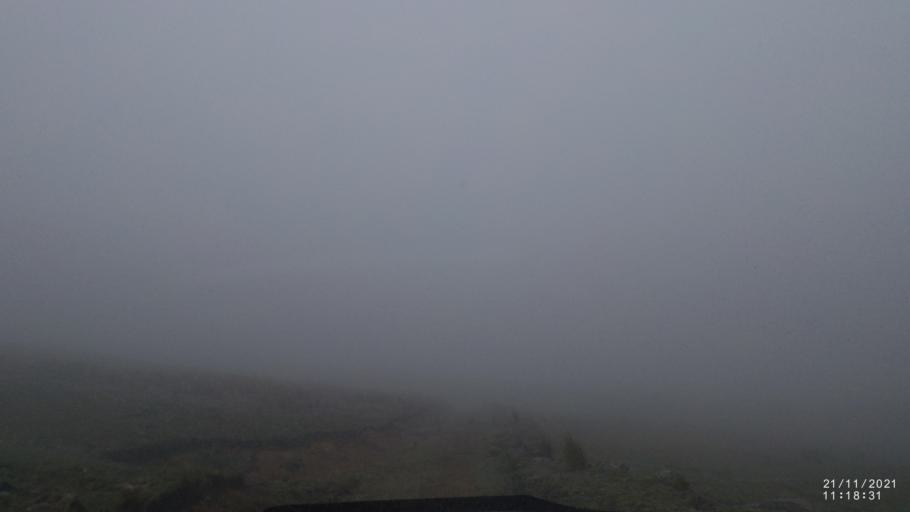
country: BO
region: Cochabamba
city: Cochabamba
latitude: -16.9632
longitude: -66.2685
